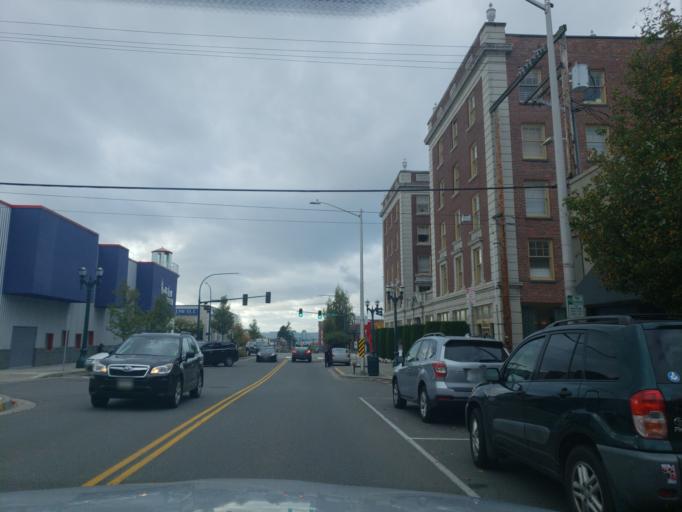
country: US
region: Washington
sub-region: Snohomish County
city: Everett
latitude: 47.9779
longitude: -122.2090
